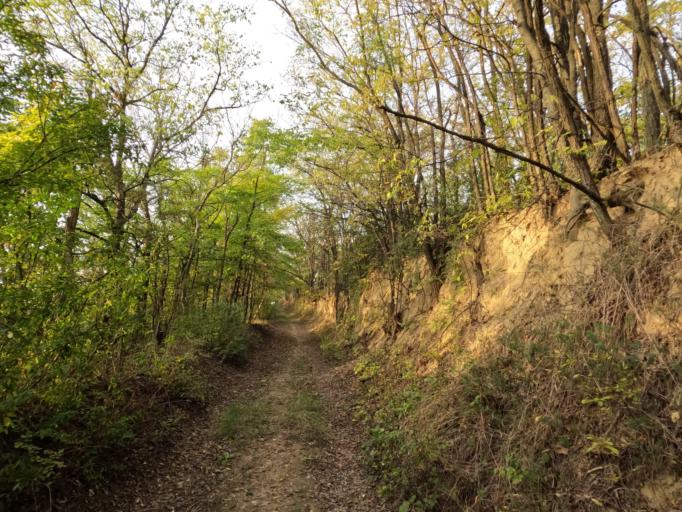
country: HU
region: Tolna
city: Szekszard
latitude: 46.3433
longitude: 18.6731
